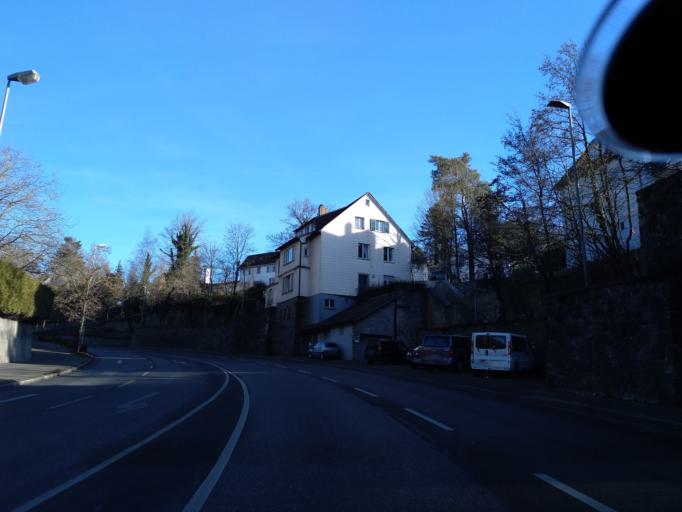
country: DE
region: Baden-Wuerttemberg
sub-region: Regierungsbezirk Stuttgart
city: Schwaebisch Hall
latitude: 49.1112
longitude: 9.7404
